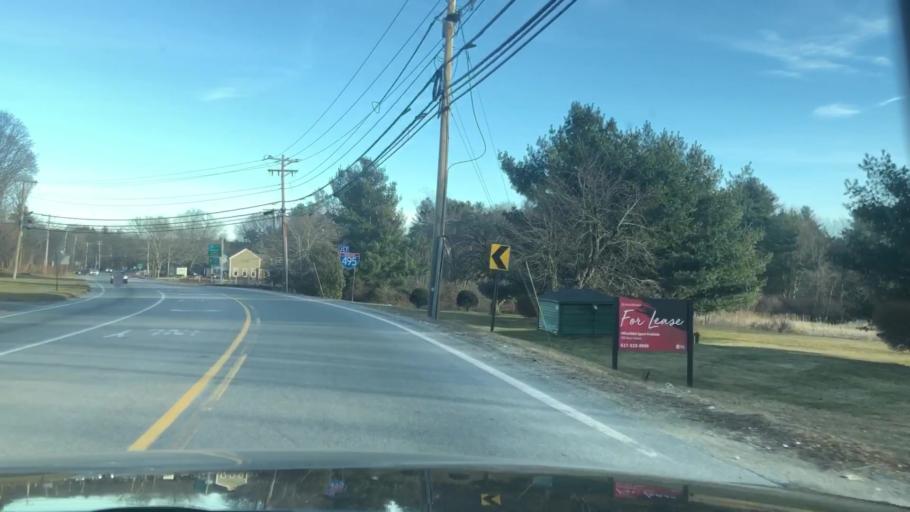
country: US
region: Massachusetts
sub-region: Worcester County
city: Bolton
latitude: 42.4310
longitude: -71.5992
